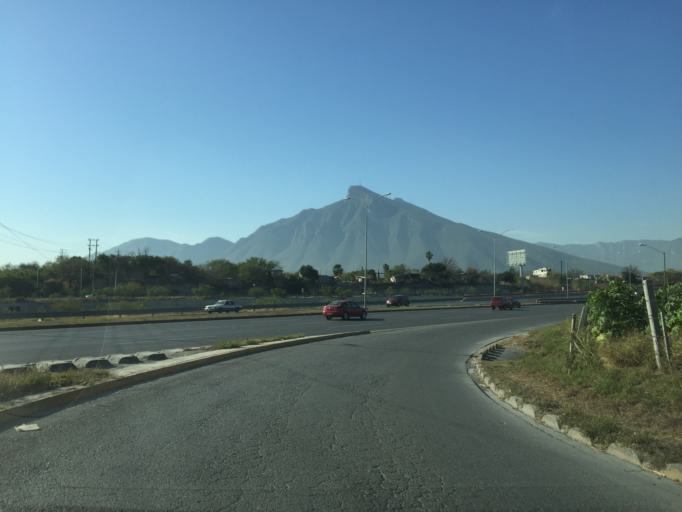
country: MX
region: Nuevo Leon
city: Guadalupe
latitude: 25.6916
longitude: -100.2173
